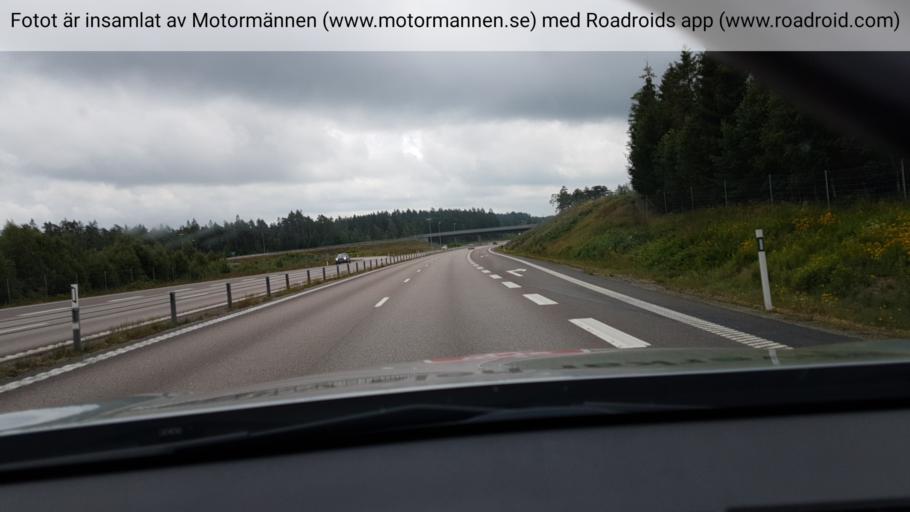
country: SE
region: Vaestra Goetaland
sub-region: Tanums Kommun
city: Tanumshede
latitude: 58.7709
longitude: 11.2750
